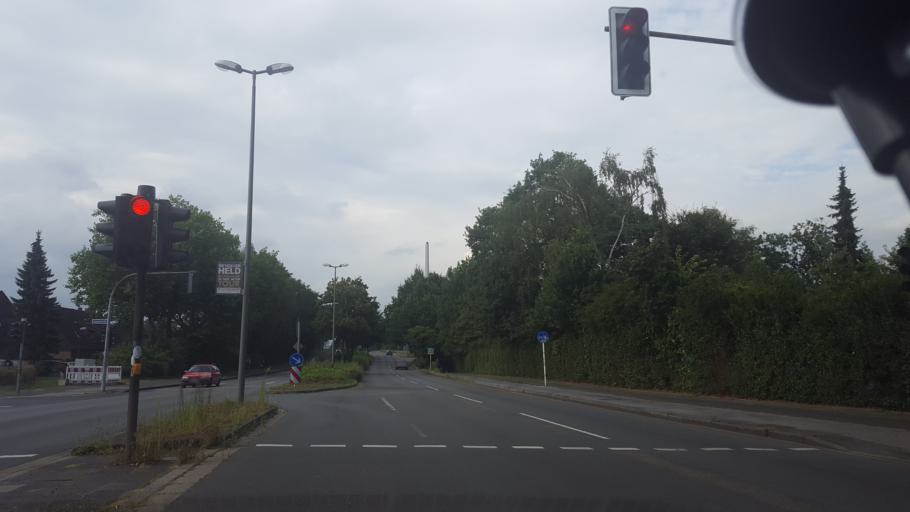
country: DE
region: North Rhine-Westphalia
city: Marl
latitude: 51.6721
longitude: 7.1029
